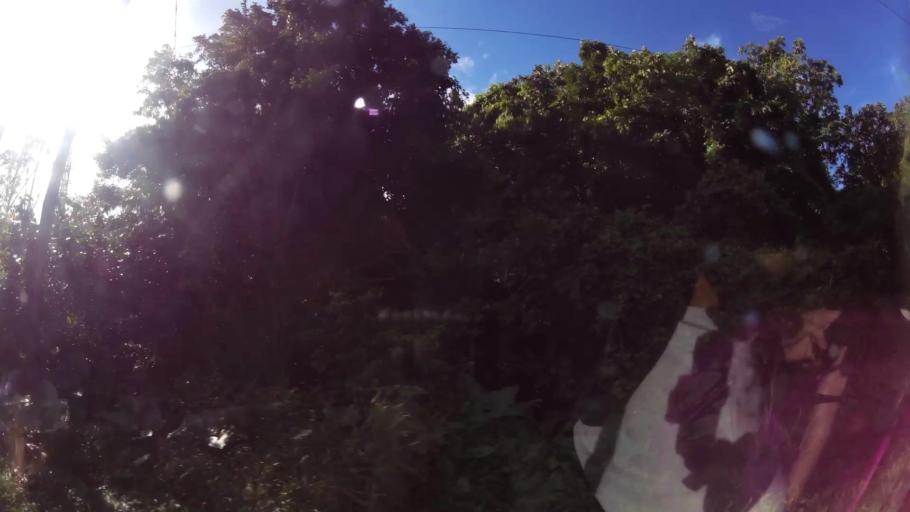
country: DM
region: Saint John
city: Portsmouth
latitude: 15.5750
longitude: -61.4449
